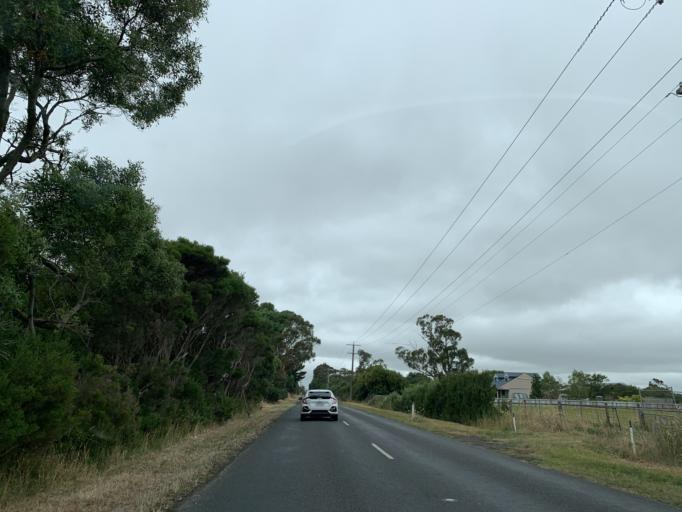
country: AU
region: Victoria
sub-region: Cardinia
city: Pakenham South
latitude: -38.1649
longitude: 145.5414
